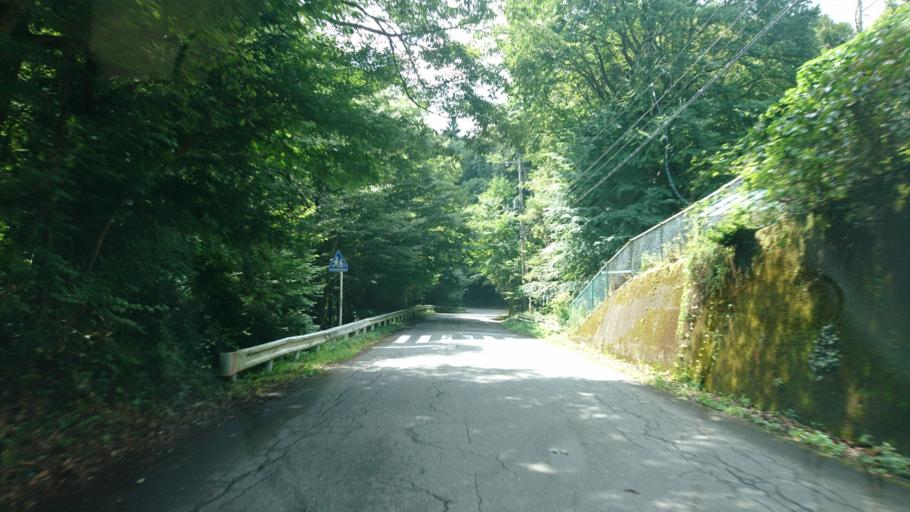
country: JP
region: Gunma
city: Omamacho-omama
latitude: 36.6082
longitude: 139.2353
